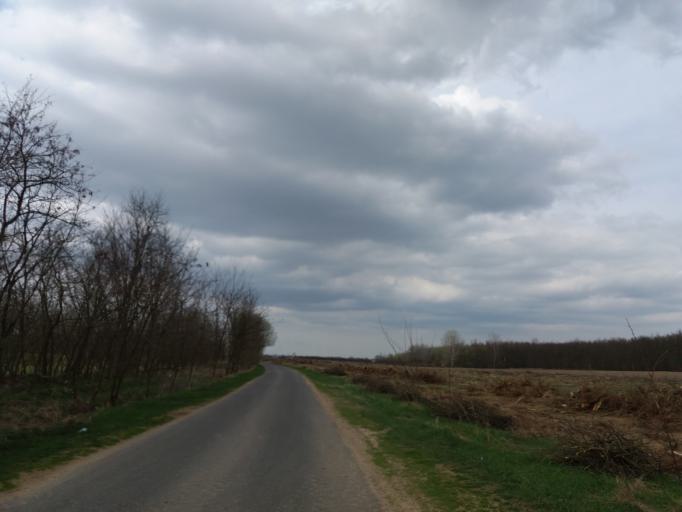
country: HU
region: Szabolcs-Szatmar-Bereg
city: Nyirtass
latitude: 48.0856
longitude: 22.0375
